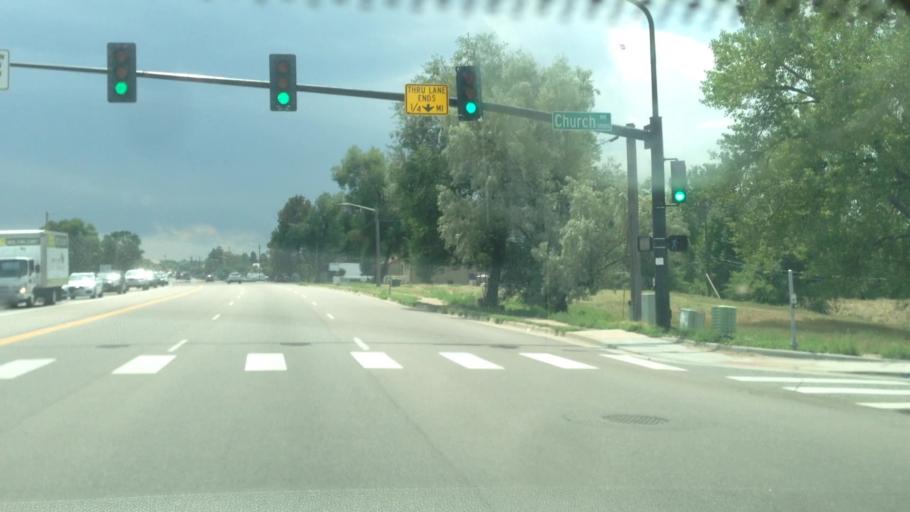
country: US
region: Colorado
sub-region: Arapahoe County
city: Littleton
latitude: 39.6103
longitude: -105.0213
